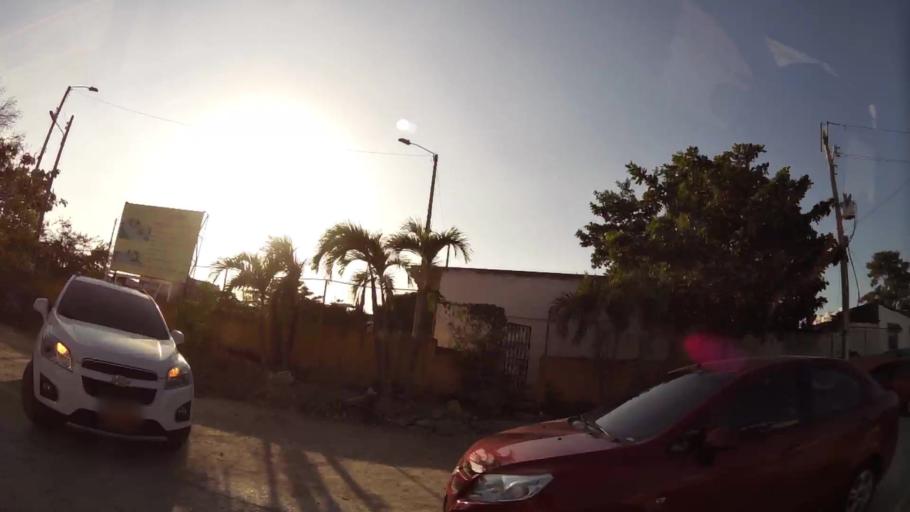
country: CO
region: Bolivar
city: Cartagena
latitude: 10.3852
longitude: -75.4780
